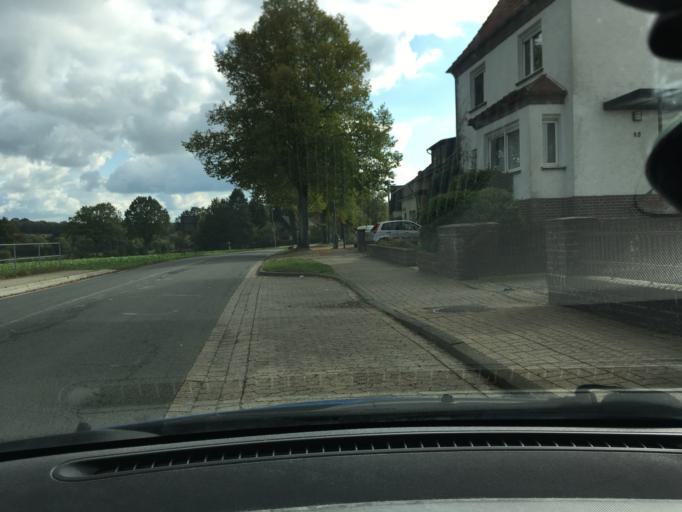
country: DE
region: Lower Saxony
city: Bad Munder am Deister
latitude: 52.1891
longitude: 9.4680
